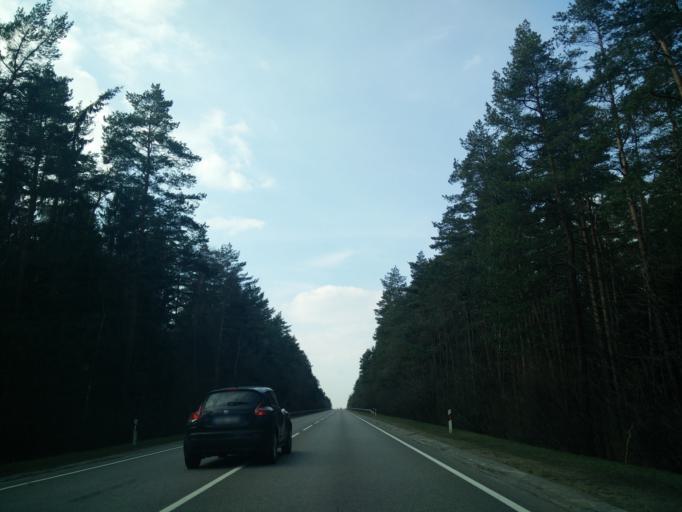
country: LT
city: Lentvaris
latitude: 54.6242
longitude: 25.0118
